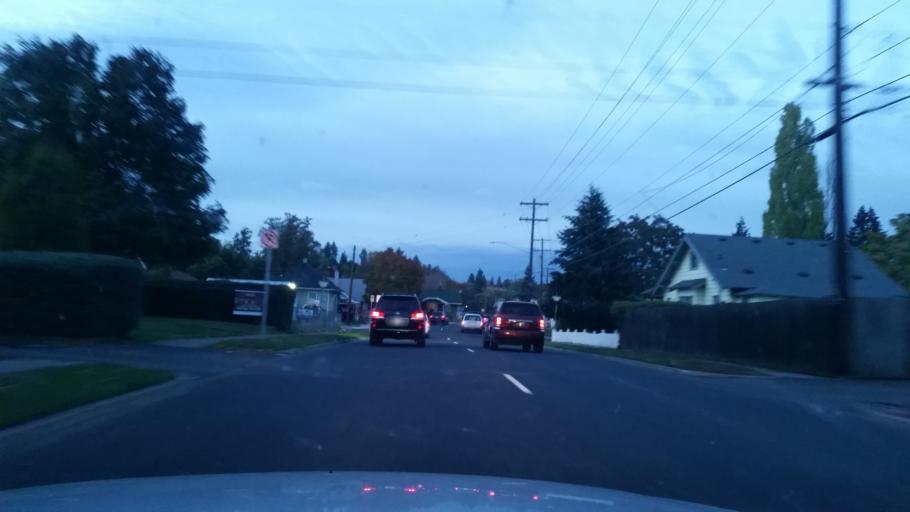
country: US
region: Washington
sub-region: Spokane County
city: Spokane
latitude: 47.6815
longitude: -117.4356
